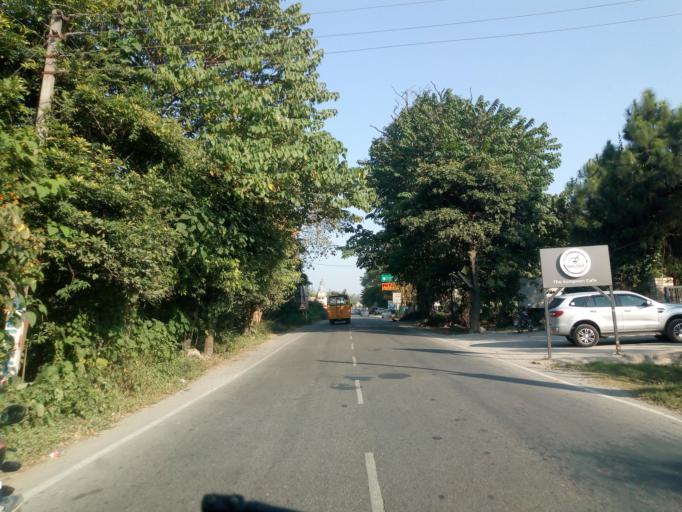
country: IN
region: Uttarakhand
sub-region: Dehradun
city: Dehradun
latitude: 30.3450
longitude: 77.9075
